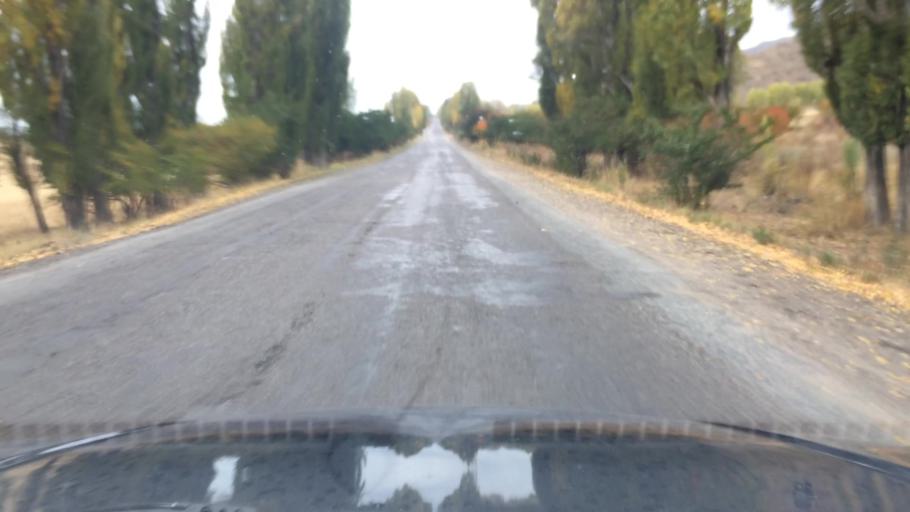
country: KG
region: Ysyk-Koel
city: Pokrovka
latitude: 42.7359
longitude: 77.9660
